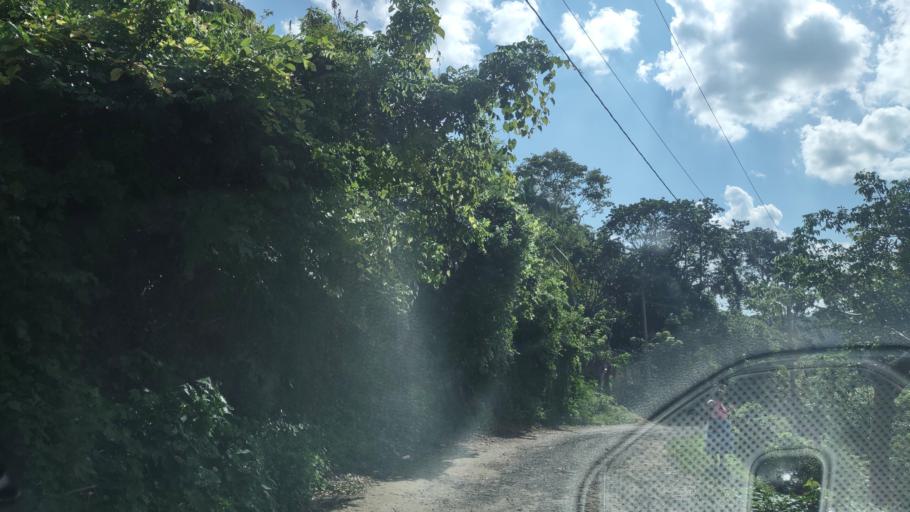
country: MM
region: Shan
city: Taunggyi
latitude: 20.5528
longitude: 97.3418
